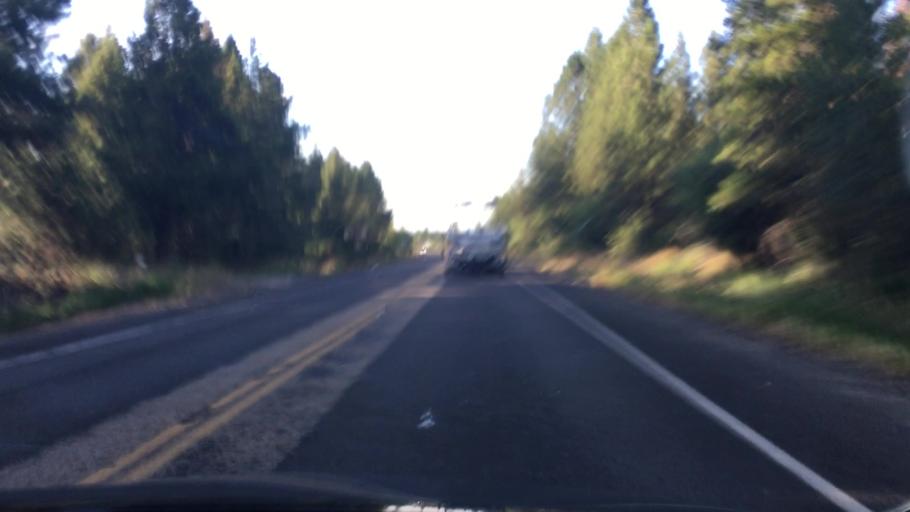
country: US
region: Idaho
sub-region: Valley County
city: Cascade
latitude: 44.6895
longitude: -116.0512
